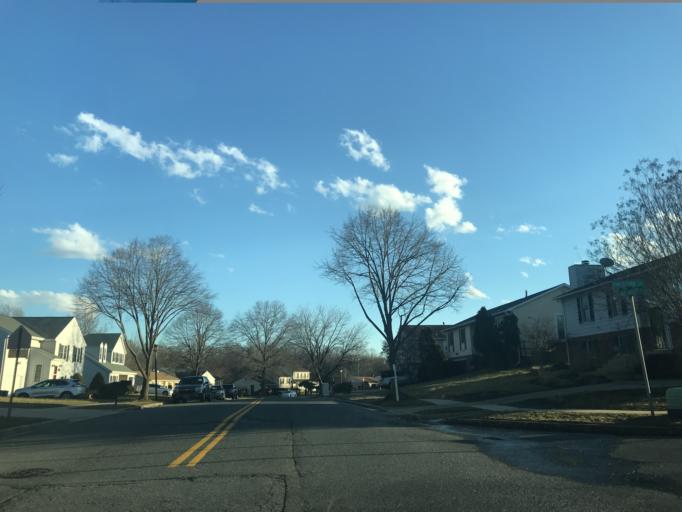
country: US
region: Maryland
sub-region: Prince George's County
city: Woodmore
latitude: 38.9059
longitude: -76.7921
